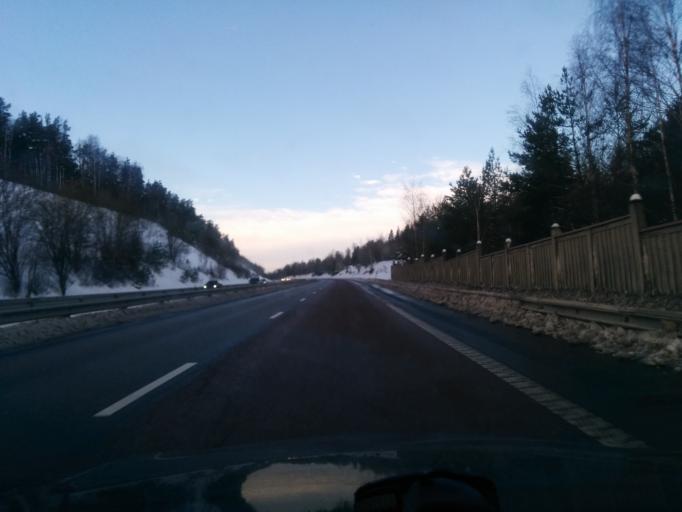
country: SE
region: Uppsala
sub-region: Habo Kommun
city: Balsta
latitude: 59.5741
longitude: 17.5448
